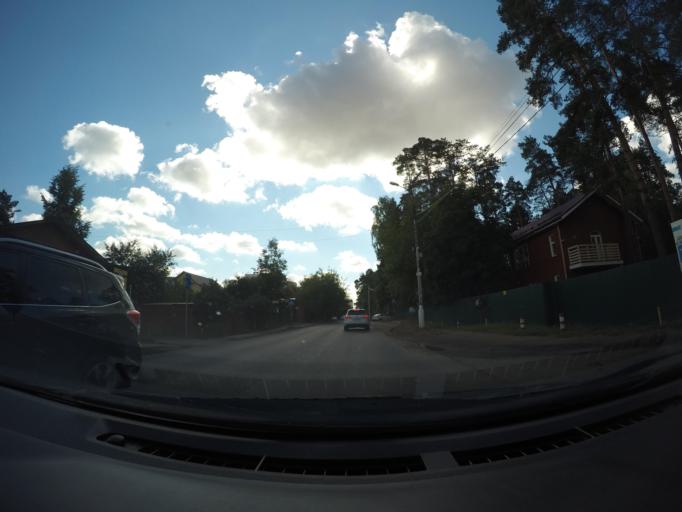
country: RU
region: Moskovskaya
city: Kratovo
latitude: 55.5857
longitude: 38.1947
